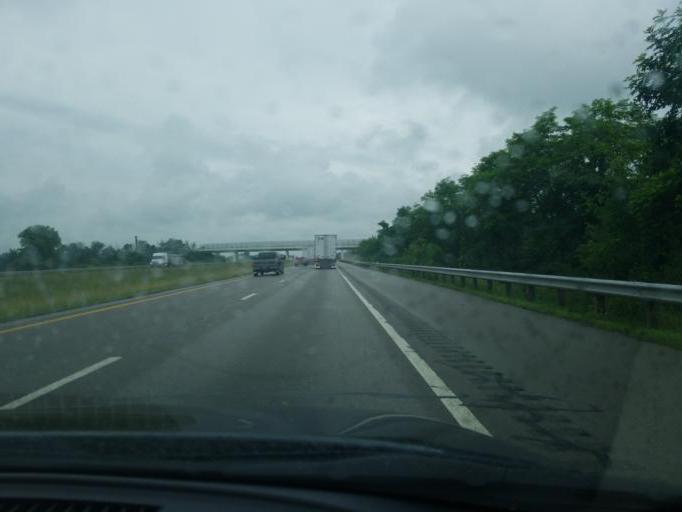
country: US
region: Ohio
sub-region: Clinton County
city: Wilmington
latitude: 39.4985
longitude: -83.9049
